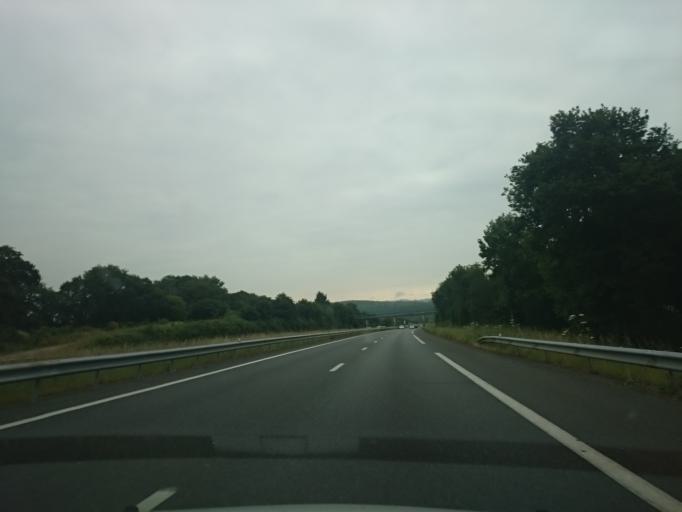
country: FR
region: Brittany
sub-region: Departement du Finistere
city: Le Faou
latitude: 48.3014
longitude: -4.1792
